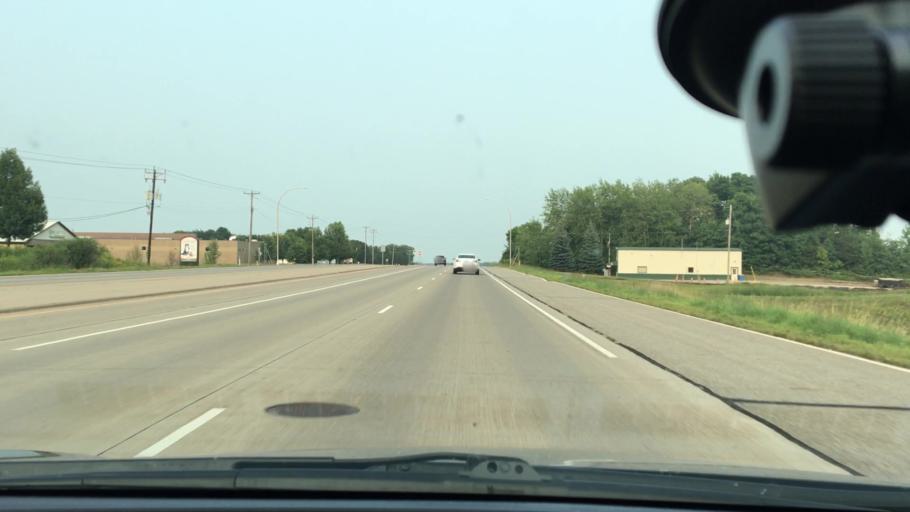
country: US
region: Minnesota
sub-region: Wright County
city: Saint Michael
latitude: 45.2109
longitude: -93.6412
